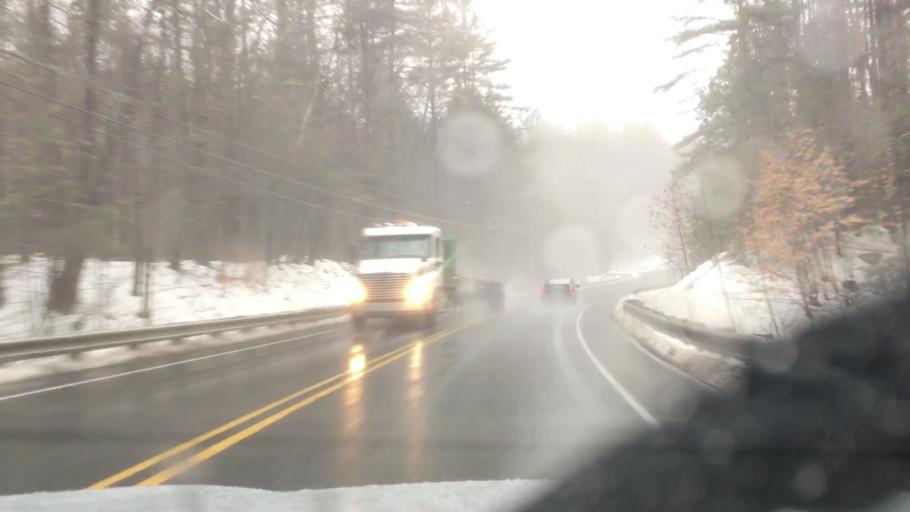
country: US
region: Massachusetts
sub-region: Franklin County
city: Wendell
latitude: 42.5166
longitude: -72.3289
